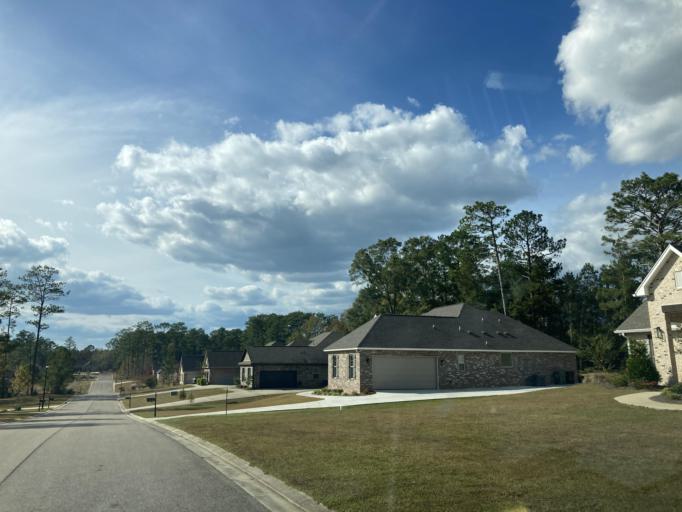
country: US
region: Mississippi
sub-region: Lamar County
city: Arnold Line
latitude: 31.3462
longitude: -89.3688
